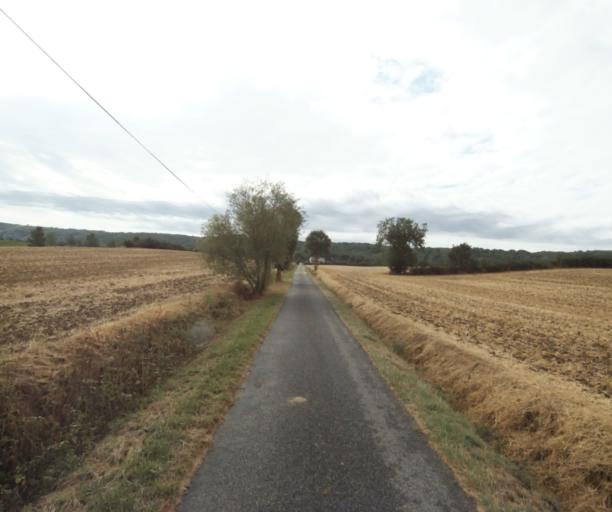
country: FR
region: Midi-Pyrenees
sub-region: Departement de la Haute-Garonne
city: Revel
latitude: 43.4192
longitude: 1.9683
